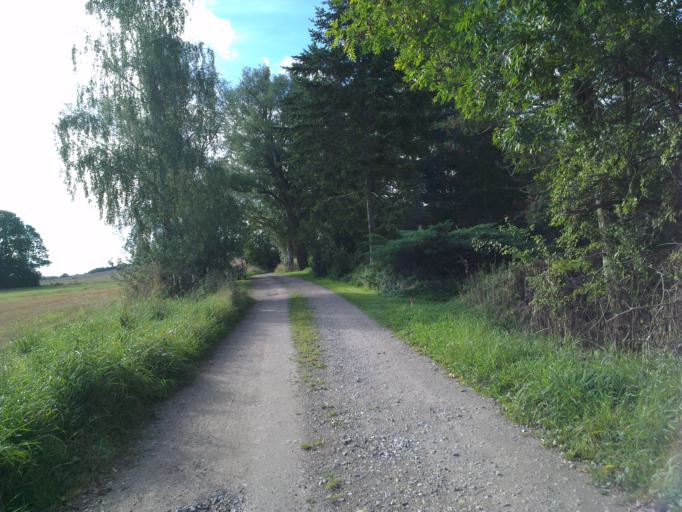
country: DK
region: Capital Region
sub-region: Frederikssund Kommune
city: Frederikssund
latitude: 55.7998
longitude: 12.0913
